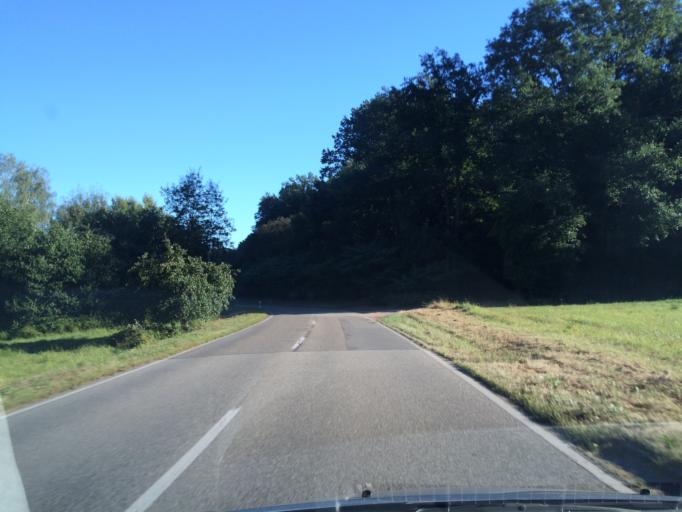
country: DE
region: Rheinland-Pfalz
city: Bruchweiler-Barenbach
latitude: 49.1302
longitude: 7.8034
